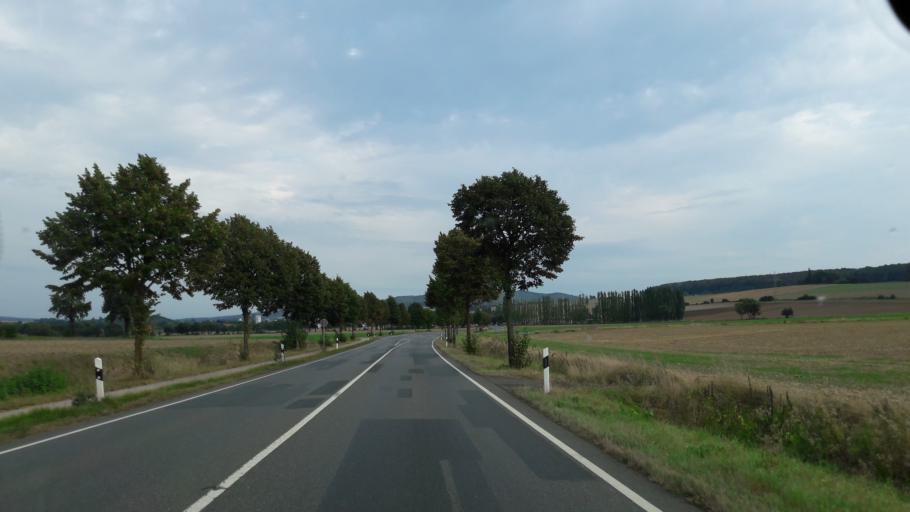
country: DE
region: Lower Saxony
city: Bad Salzdetfurth
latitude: 52.0987
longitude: 9.9941
